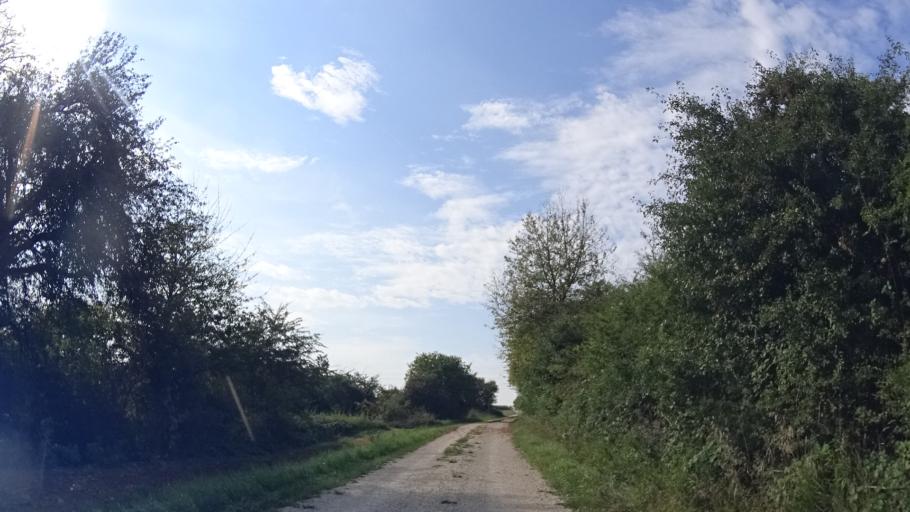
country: DE
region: Bavaria
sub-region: Lower Bavaria
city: Riedenburg
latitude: 48.9631
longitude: 11.6715
